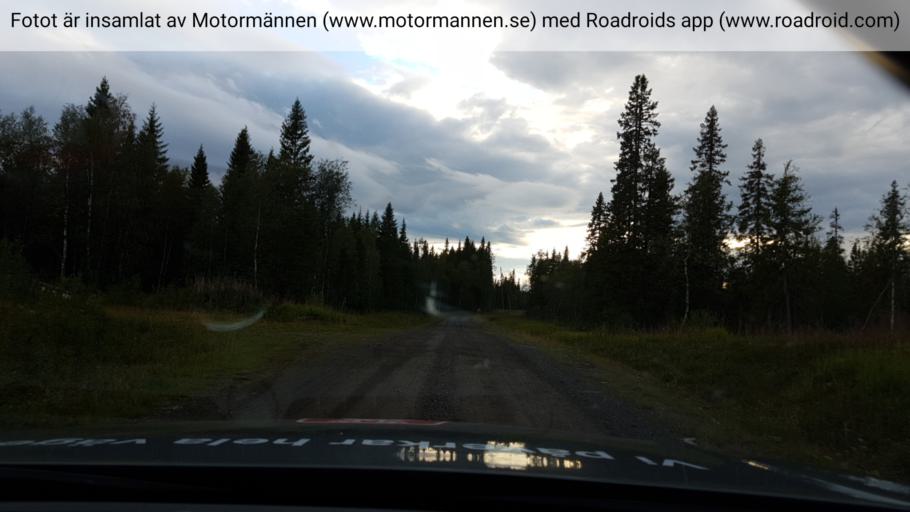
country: SE
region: Jaemtland
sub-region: OEstersunds Kommun
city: Lit
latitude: 63.4942
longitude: 15.1951
